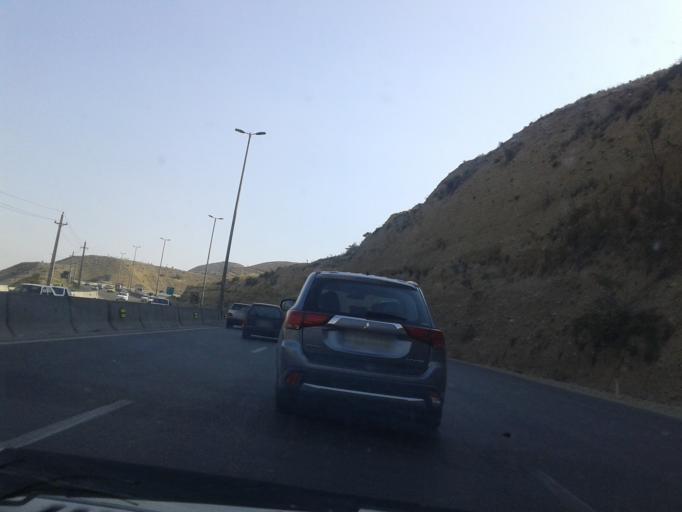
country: IR
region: Tehran
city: Pakdasht
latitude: 35.7393
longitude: 51.6914
